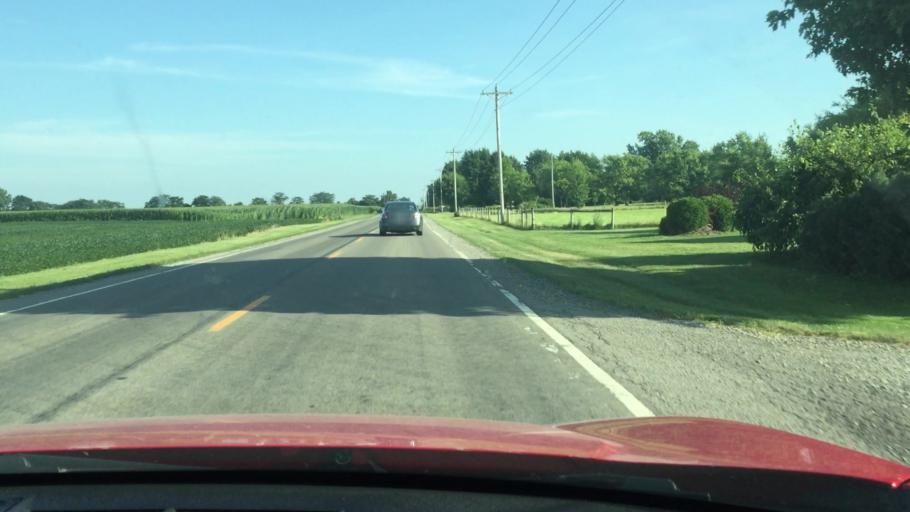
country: US
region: Ohio
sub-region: Hardin County
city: Ada
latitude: 40.6575
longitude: -83.8503
